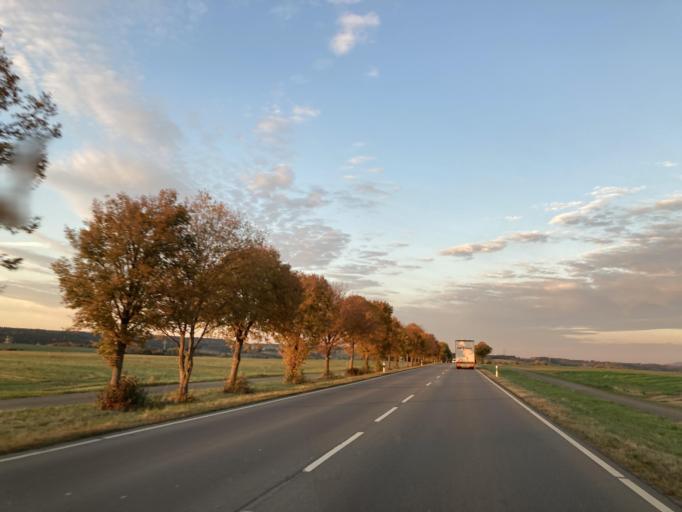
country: DE
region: Baden-Wuerttemberg
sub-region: Tuebingen Region
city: Dotternhausen
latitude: 48.2361
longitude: 8.7976
